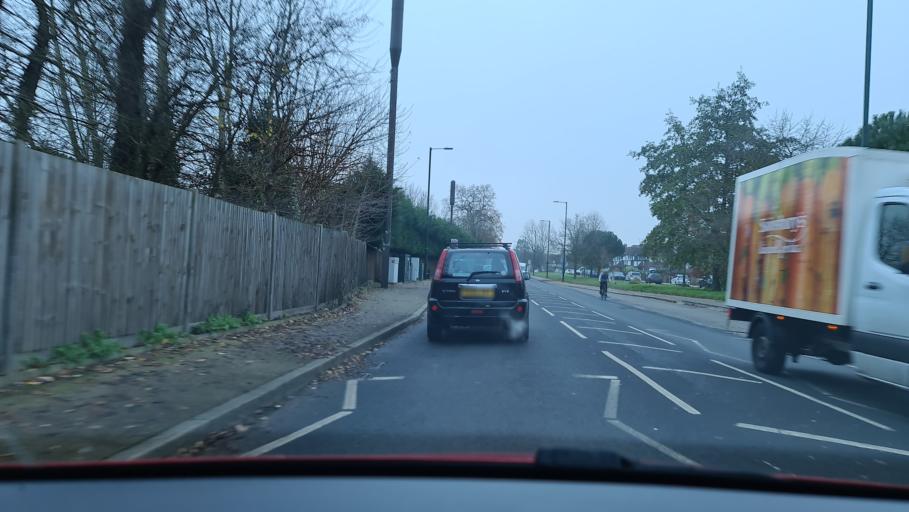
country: GB
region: England
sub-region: Greater London
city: Richmond
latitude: 51.4405
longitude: -0.3036
